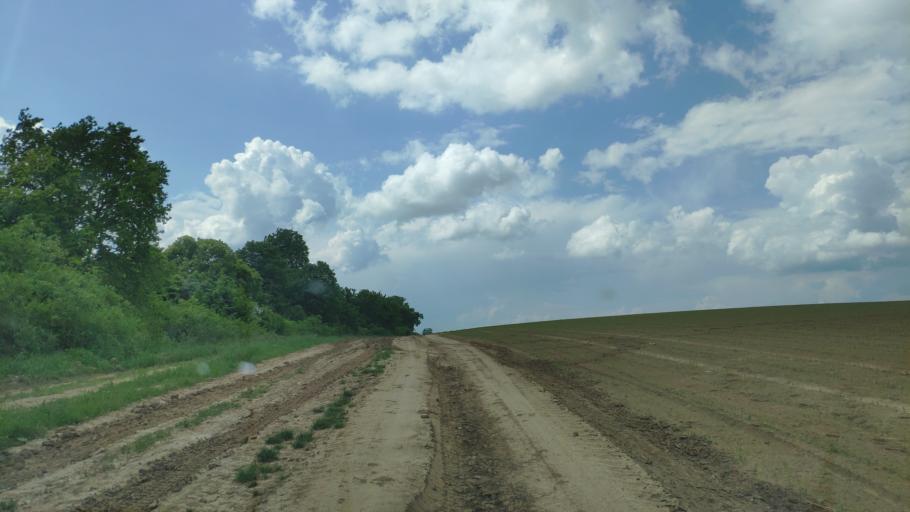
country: SK
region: Presovsky
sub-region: Okres Presov
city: Presov
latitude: 49.0271
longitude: 21.1735
